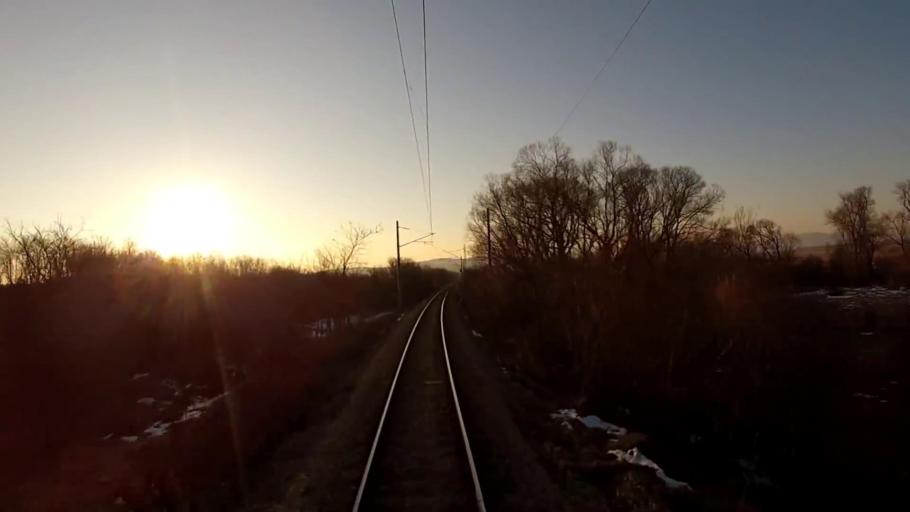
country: BG
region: Sofiya
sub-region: Obshtina Slivnitsa
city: Slivnitsa
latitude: 42.8829
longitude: 22.9821
